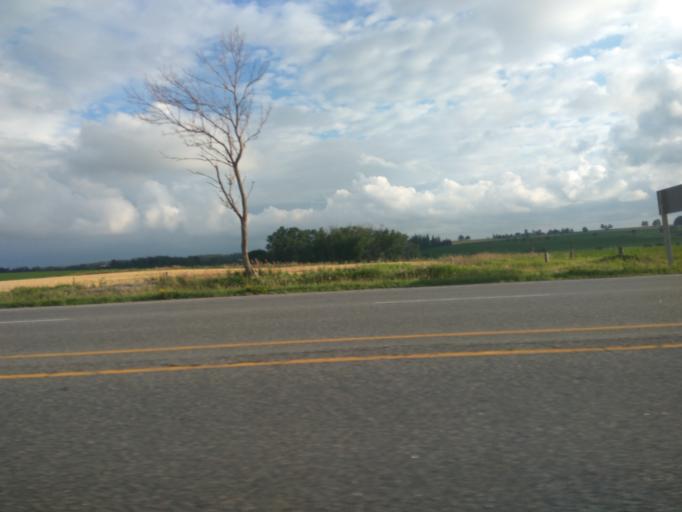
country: CA
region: Ontario
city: Stratford
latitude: 43.3659
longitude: -80.7297
